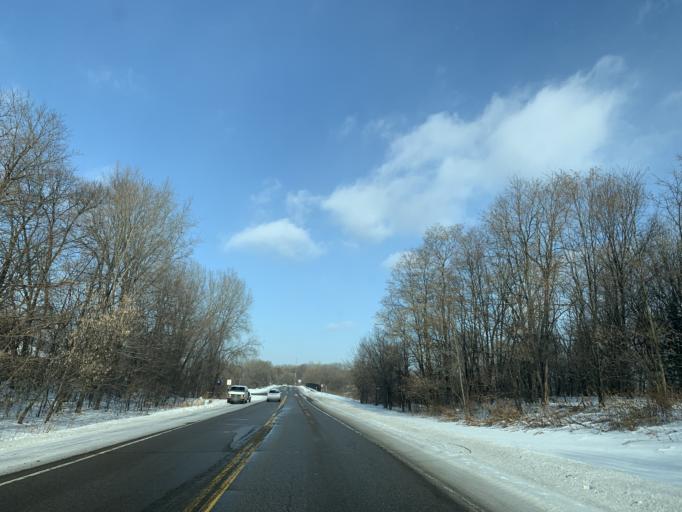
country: US
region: Minnesota
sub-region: Dakota County
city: Inver Grove Heights
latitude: 44.8723
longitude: -93.0645
